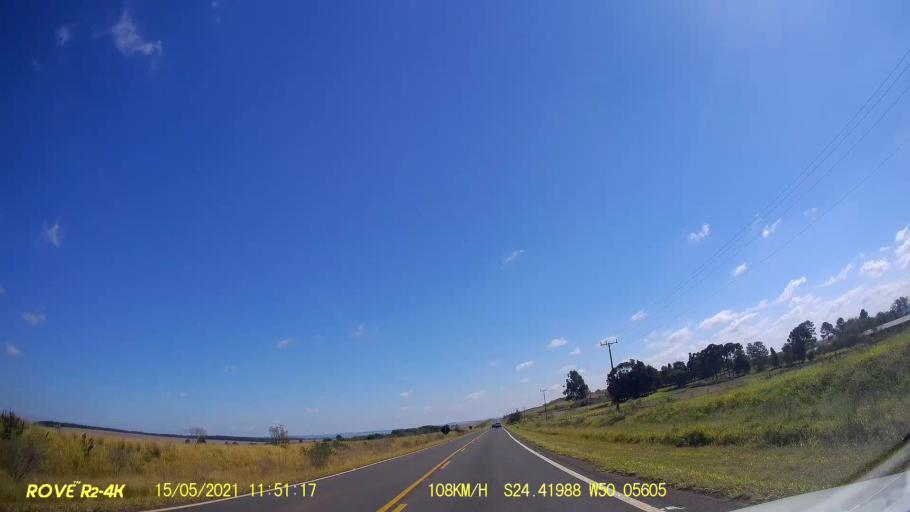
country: BR
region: Parana
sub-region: Pirai Do Sul
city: Pirai do Sul
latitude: -24.4199
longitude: -50.0559
